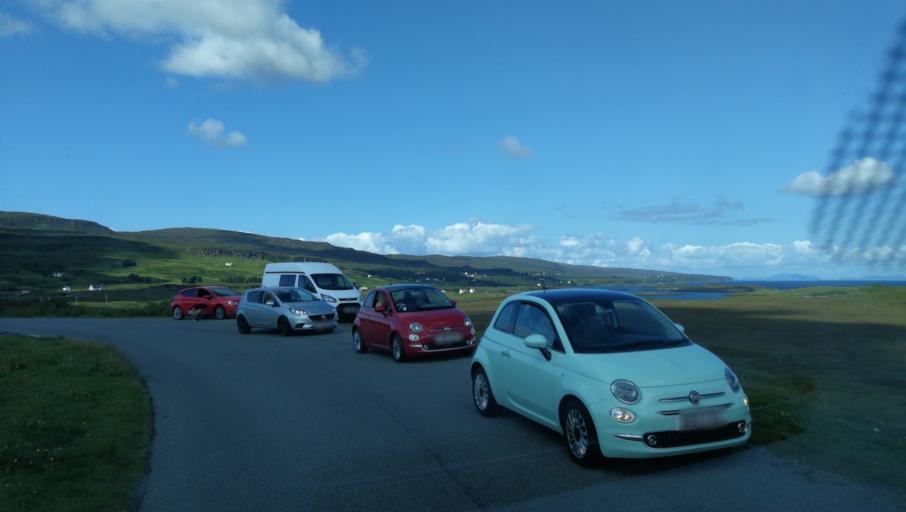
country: GB
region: Scotland
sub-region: Highland
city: Isle of Skye
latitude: 57.4293
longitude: -6.6097
